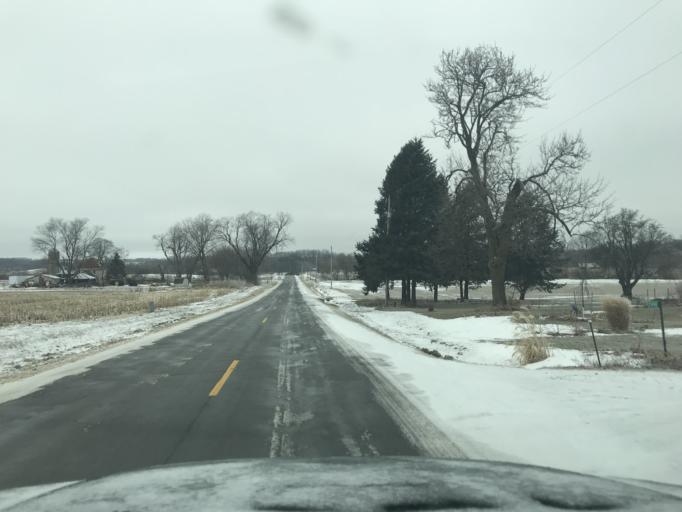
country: US
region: Wisconsin
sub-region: Dane County
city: Cottage Grove
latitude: 43.1039
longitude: -89.2365
